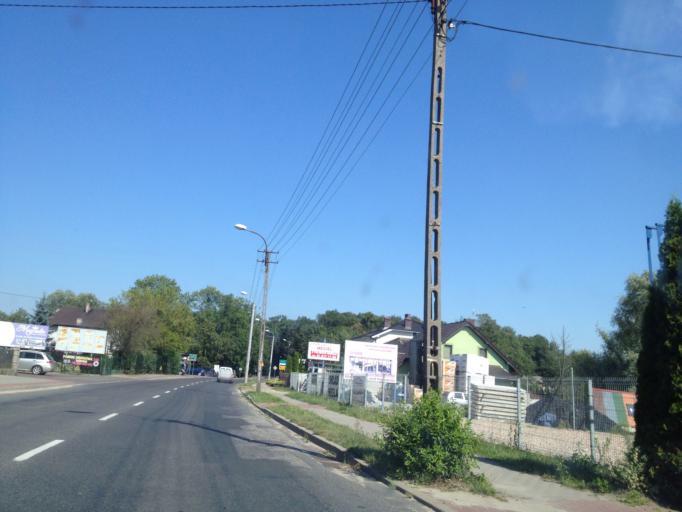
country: PL
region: Greater Poland Voivodeship
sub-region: Powiat poznanski
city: Kornik
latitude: 52.2356
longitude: 17.0940
